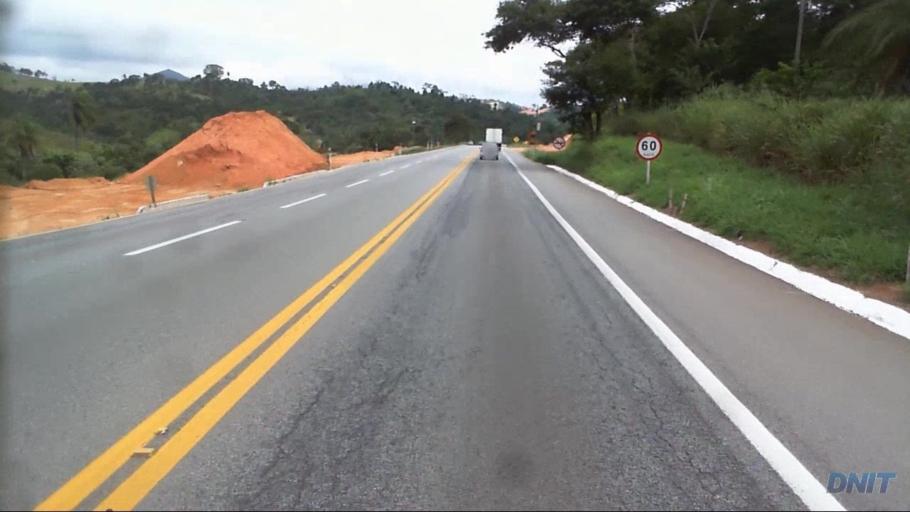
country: BR
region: Minas Gerais
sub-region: Caete
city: Caete
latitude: -19.7450
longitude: -43.6168
